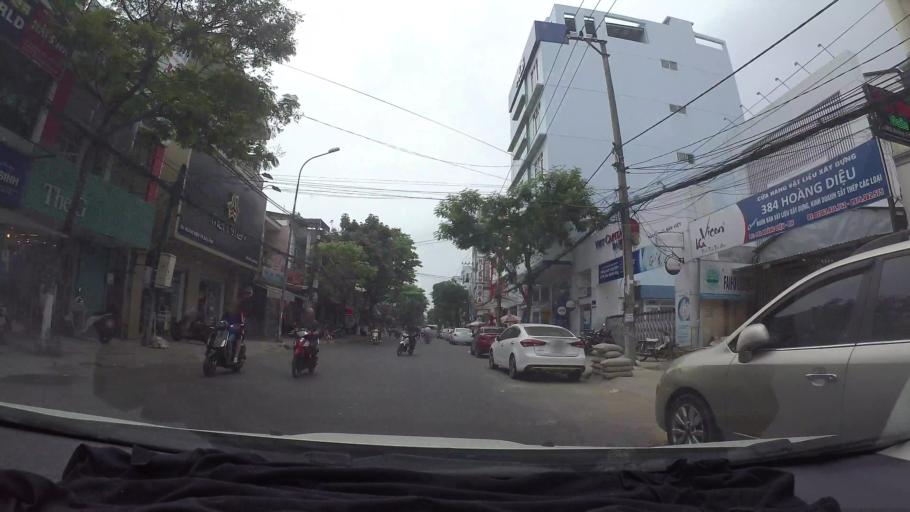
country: VN
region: Da Nang
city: Da Nang
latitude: 16.0558
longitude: 108.2172
